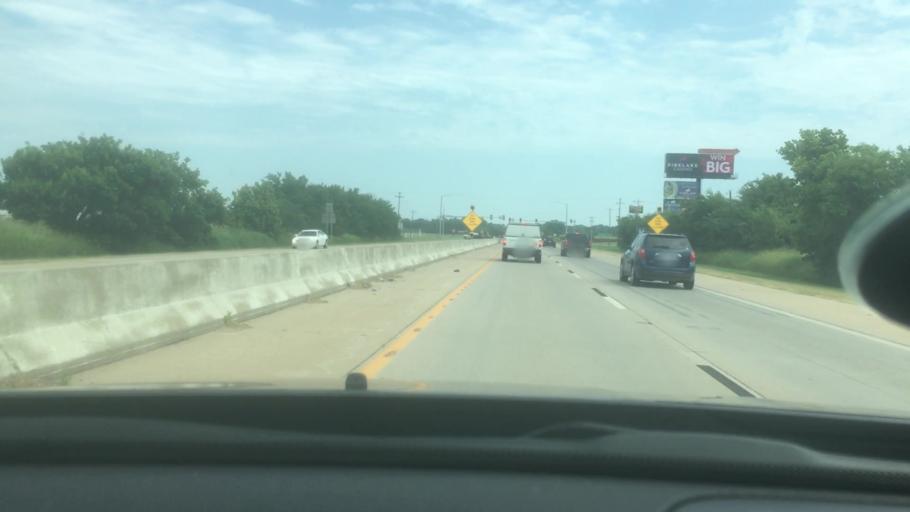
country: US
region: Oklahoma
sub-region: Pottawatomie County
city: Shawnee
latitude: 35.3019
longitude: -96.9435
